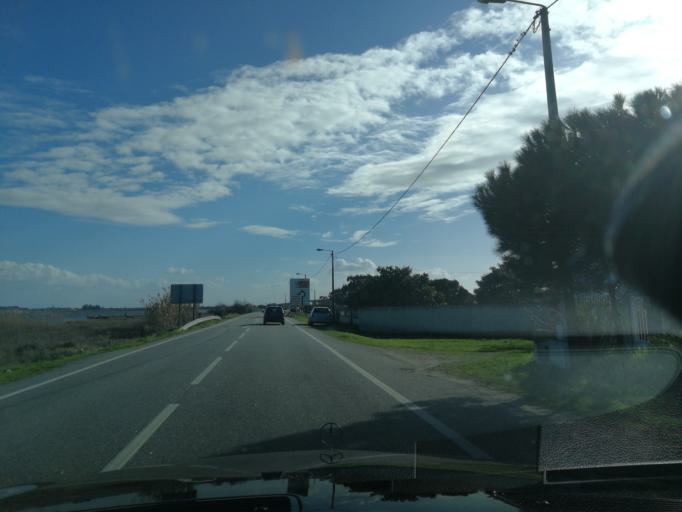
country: PT
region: Aveiro
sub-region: Estarreja
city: Pardilho
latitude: 40.7975
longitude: -8.6738
